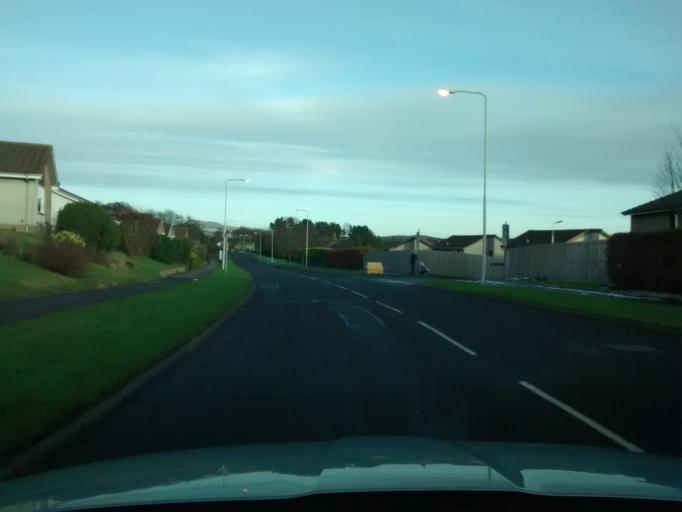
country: GB
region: Scotland
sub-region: Fife
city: Inverkeithing
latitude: 56.0288
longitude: -3.3579
